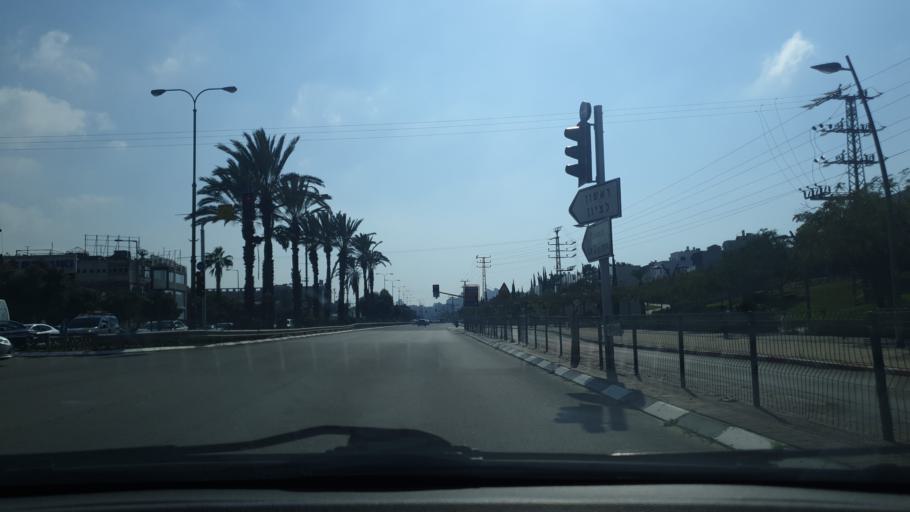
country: IL
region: Central District
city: Bet Dagan
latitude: 31.9837
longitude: 34.8101
